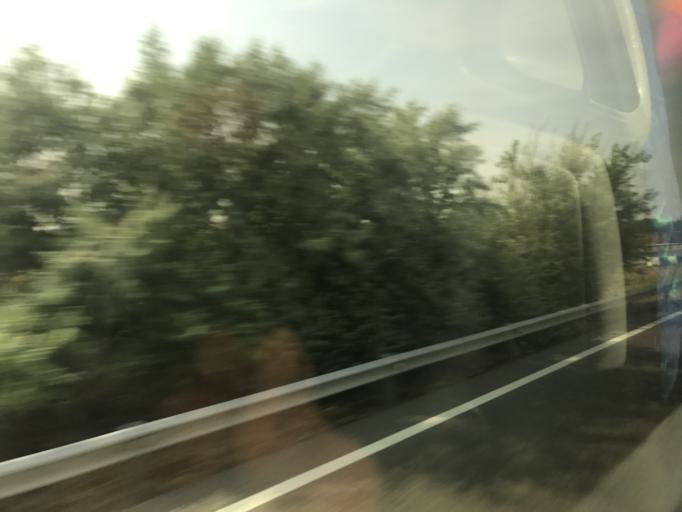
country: ES
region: Castille and Leon
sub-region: Provincia de Palencia
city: Villodrigo
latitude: 42.1583
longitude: -4.0803
